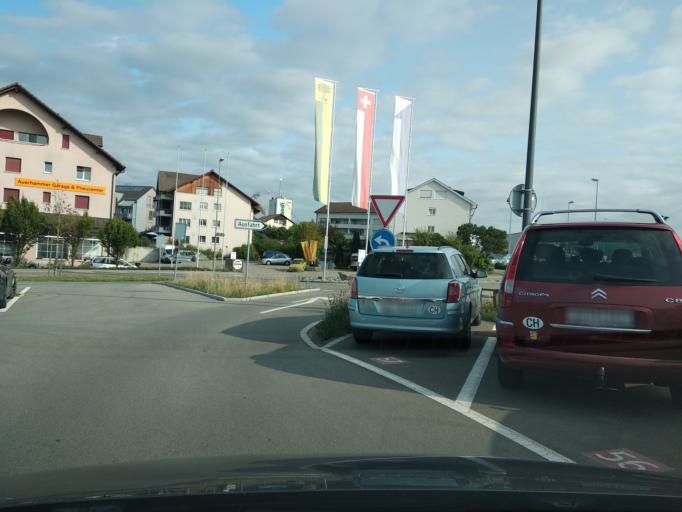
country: CH
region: Zurich
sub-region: Bezirk Andelfingen
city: Marthalen
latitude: 47.6321
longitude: 8.6567
